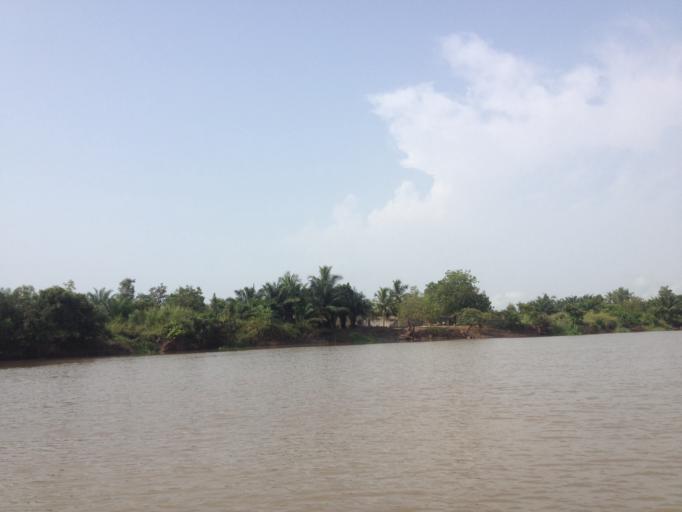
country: BJ
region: Mono
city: Grand-Popo
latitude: 6.3321
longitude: 1.7870
